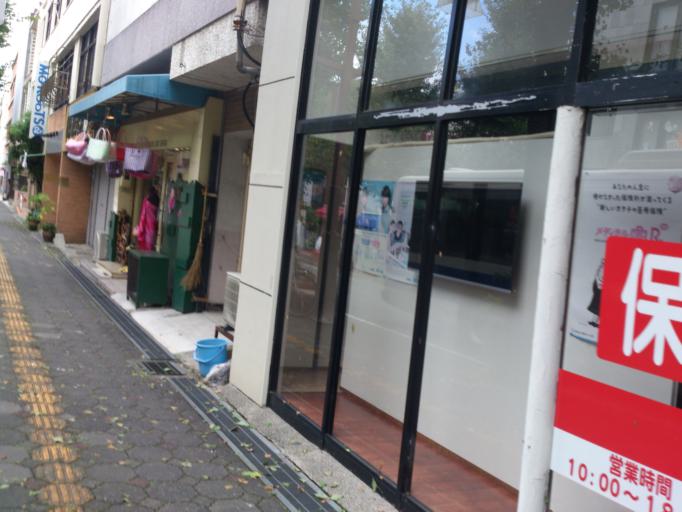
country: JP
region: Yamaguchi
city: Yamaguchi-shi
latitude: 34.1765
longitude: 131.4768
